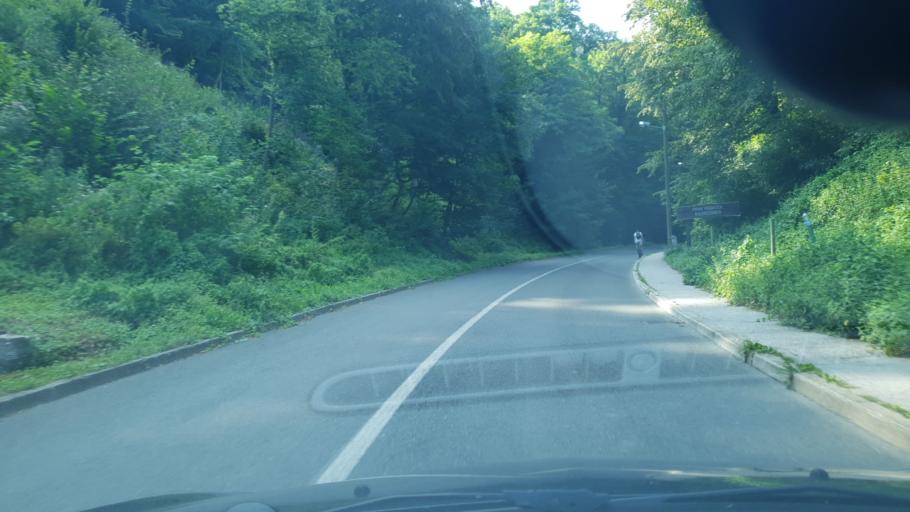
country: HR
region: Grad Zagreb
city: Zagreb
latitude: 45.8664
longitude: 15.9792
